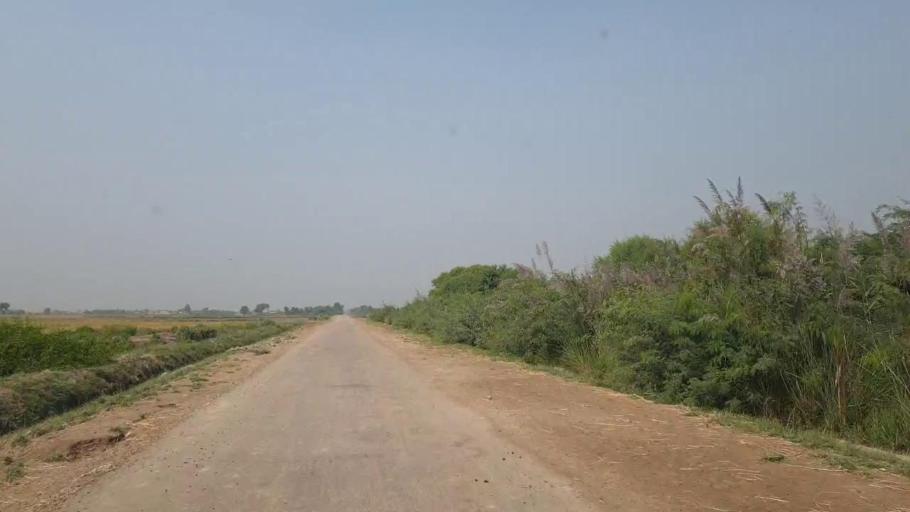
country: PK
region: Sindh
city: Matli
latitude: 25.1451
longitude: 68.7045
